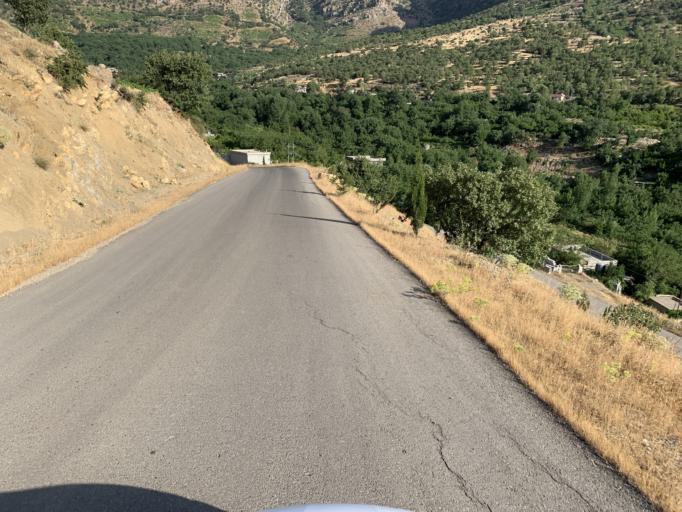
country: IQ
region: As Sulaymaniyah
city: Qeladize
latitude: 35.9929
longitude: 45.1951
